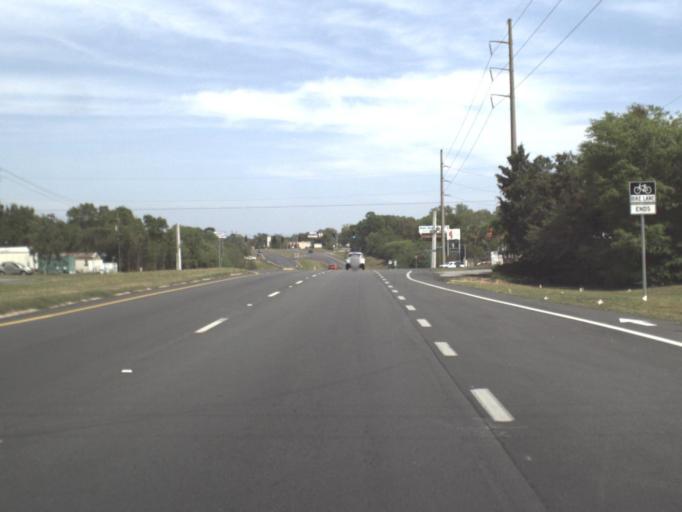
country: US
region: Florida
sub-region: Escambia County
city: Ferry Pass
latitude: 30.5319
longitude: -87.2162
